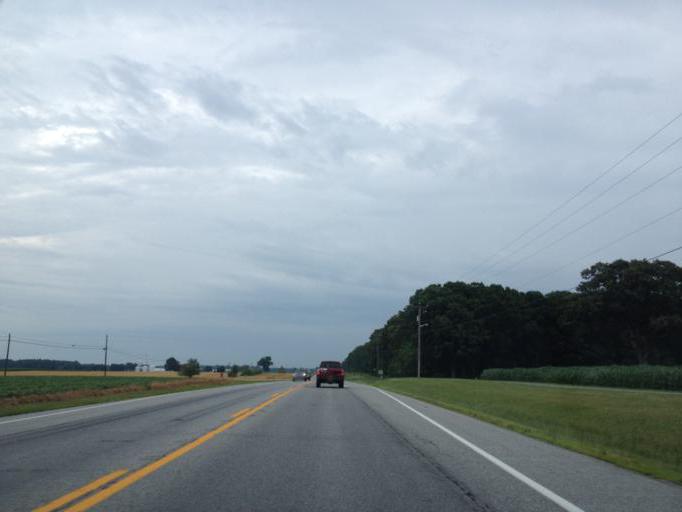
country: US
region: Maryland
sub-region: Queen Anne's County
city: Centreville
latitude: 38.9303
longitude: -76.0141
